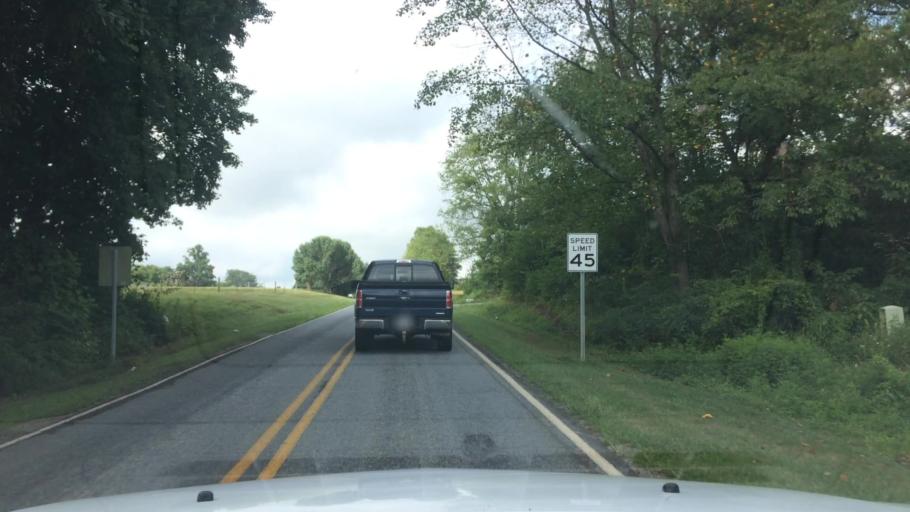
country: US
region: North Carolina
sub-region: Yadkin County
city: Jonesville
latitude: 36.1051
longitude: -80.8587
